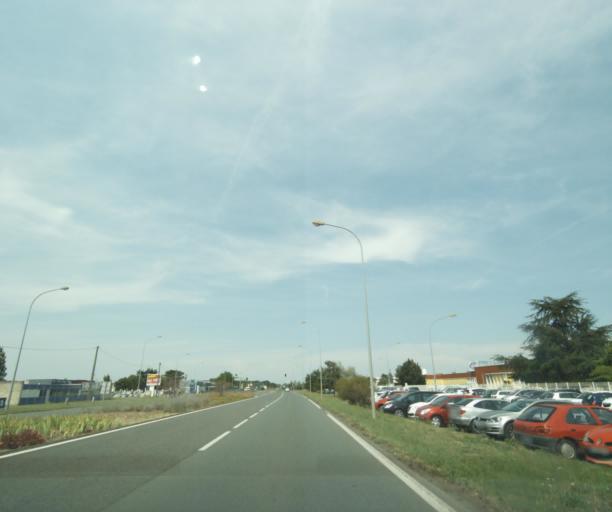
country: FR
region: Poitou-Charentes
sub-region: Departement de la Vienne
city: Antran
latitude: 46.8433
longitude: 0.5492
